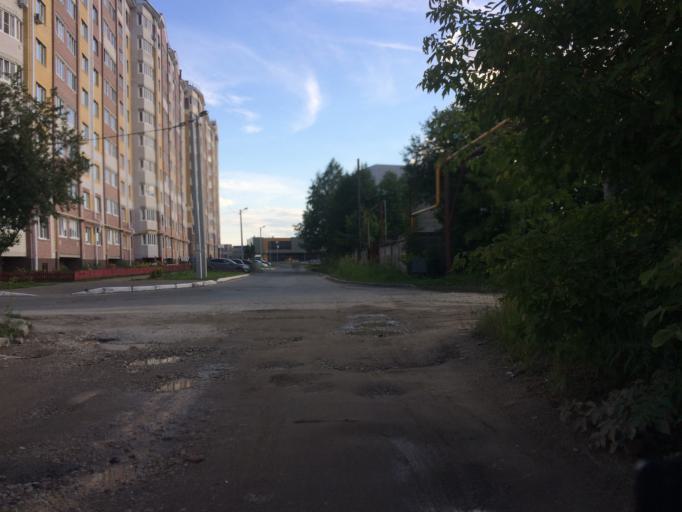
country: RU
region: Mariy-El
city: Yoshkar-Ola
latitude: 56.6345
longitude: 47.9367
